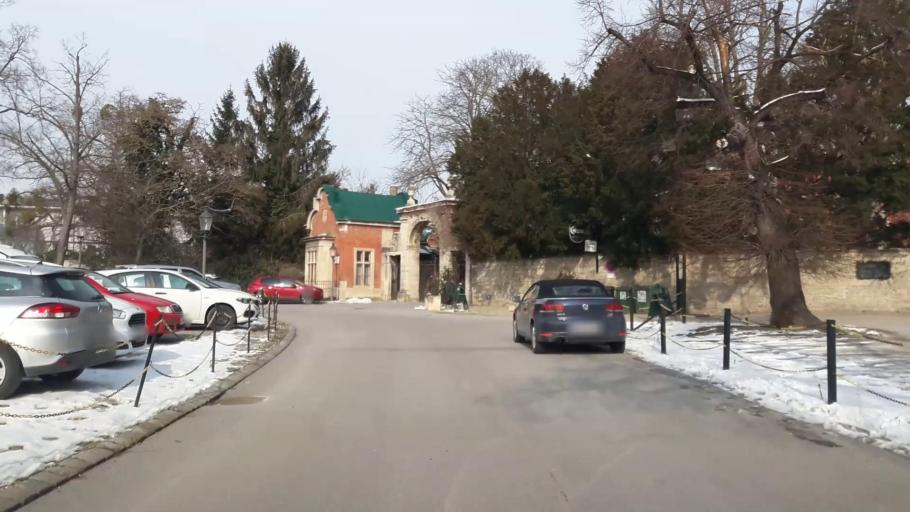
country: AT
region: Burgenland
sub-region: Politischer Bezirk Neusiedl am See
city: Bruckneudorf
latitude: 48.0251
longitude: 16.7815
